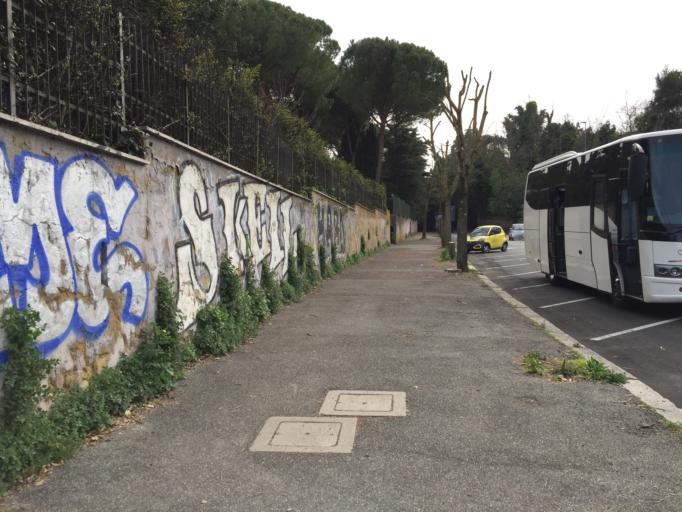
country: VA
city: Vatican City
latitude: 41.8915
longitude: 12.4586
